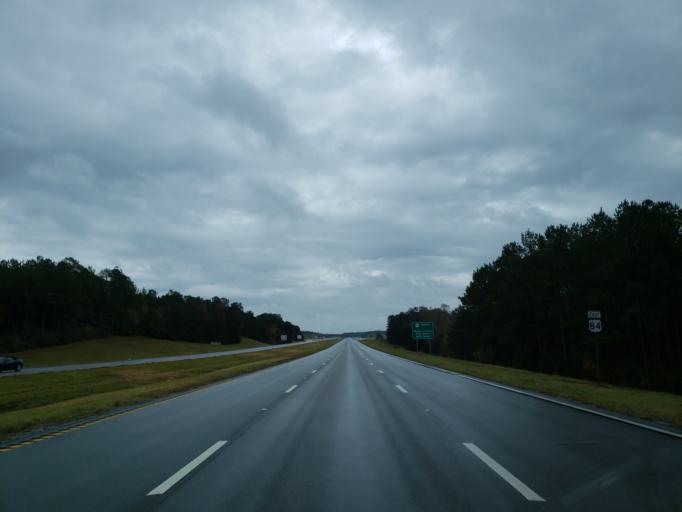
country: US
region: Mississippi
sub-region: Wayne County
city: Waynesboro
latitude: 31.7052
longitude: -88.6400
